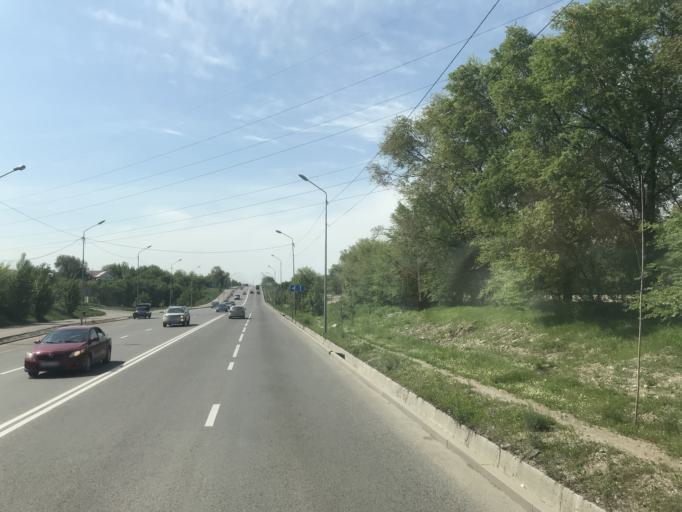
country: KZ
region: Almaty Qalasy
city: Almaty
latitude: 43.3034
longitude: 76.8895
